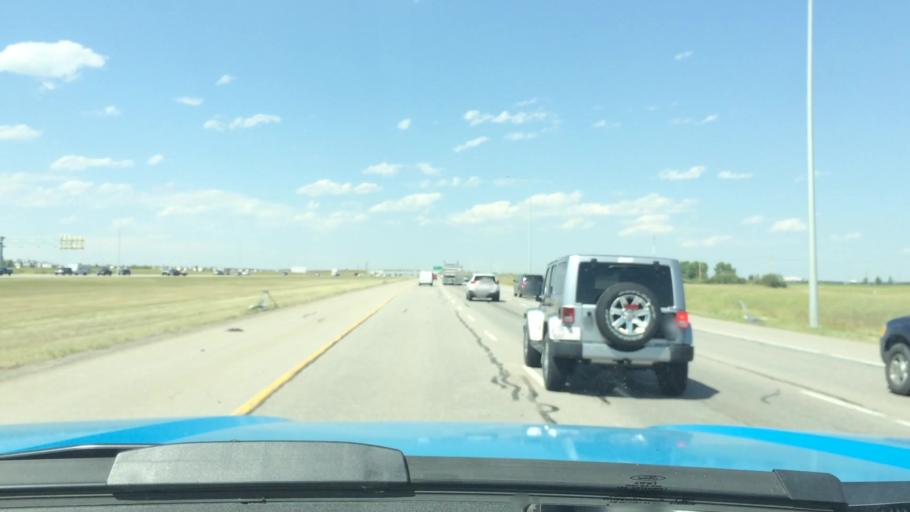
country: CA
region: Alberta
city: Chestermere
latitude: 51.0824
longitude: -113.9199
